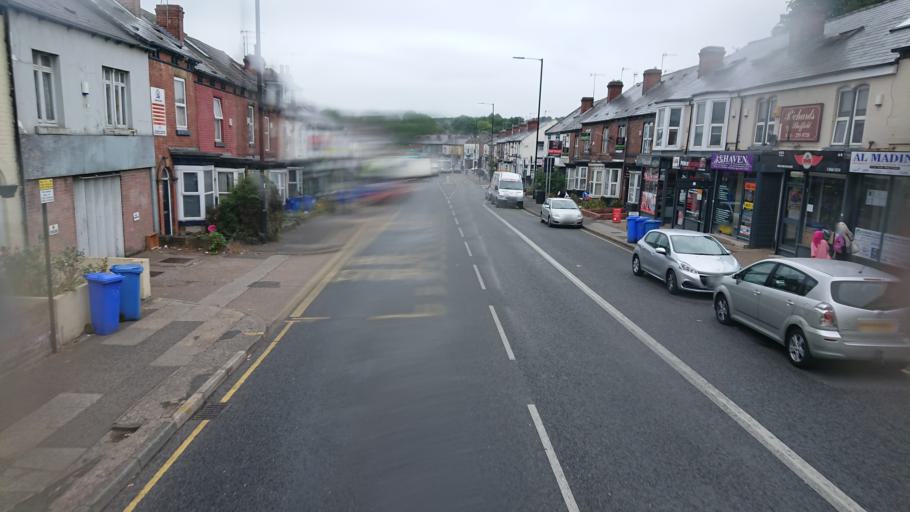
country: GB
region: England
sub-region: Sheffield
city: Sheffield
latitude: 53.3644
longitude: -1.4755
